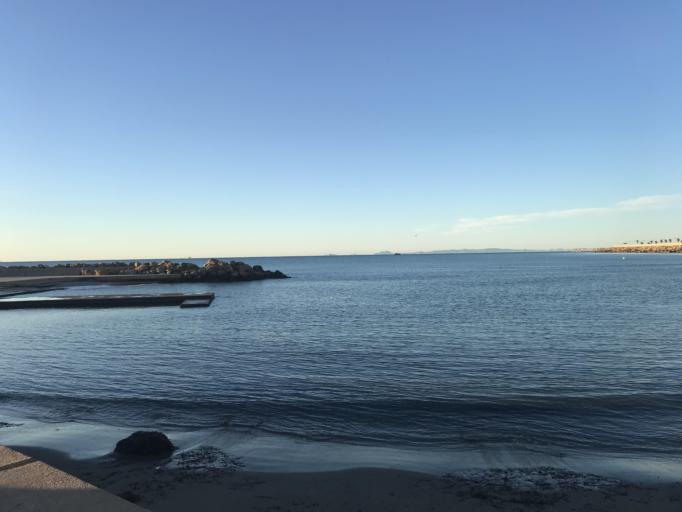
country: ES
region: Valencia
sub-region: Provincia de Alicante
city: Torrevieja
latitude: 37.9749
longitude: -0.6753
